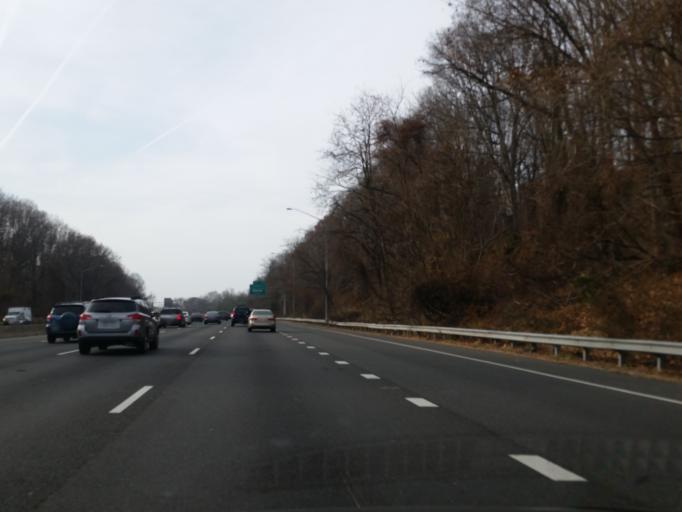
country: US
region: Maryland
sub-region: Montgomery County
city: Cabin John
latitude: 38.9835
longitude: -77.1631
